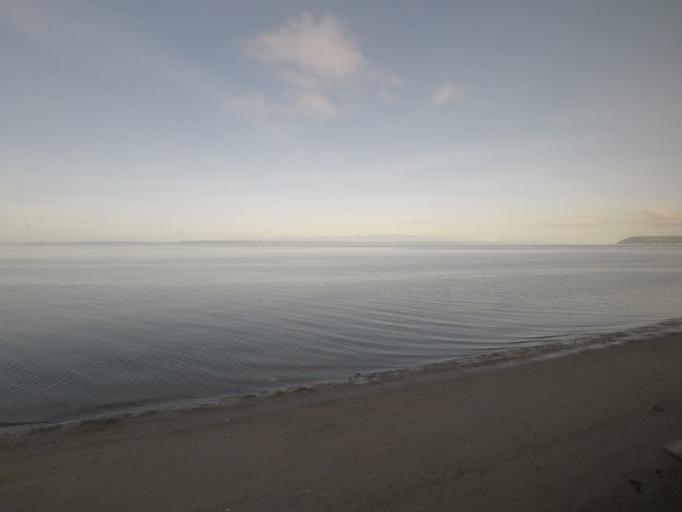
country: US
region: Washington
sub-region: Snohomish County
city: Meadowdale
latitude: 47.8776
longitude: -122.3310
